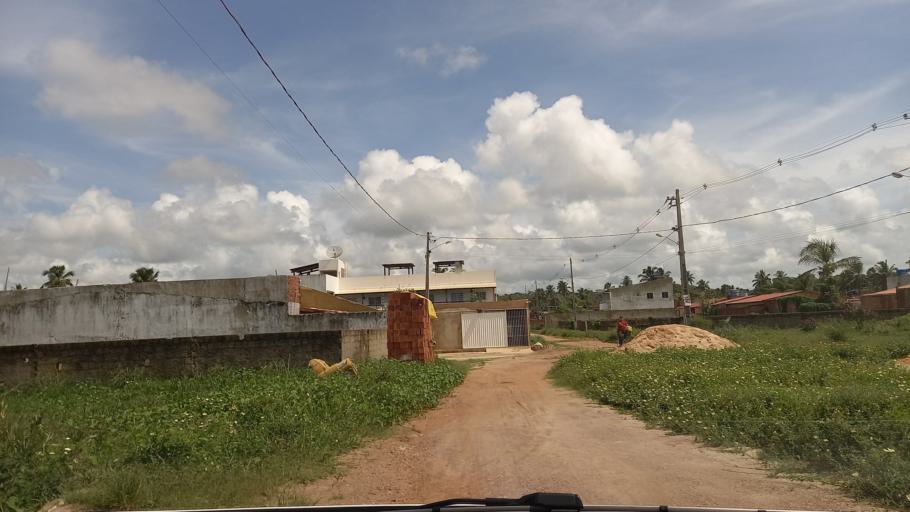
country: BR
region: Pernambuco
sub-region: Sao Jose Da Coroa Grande
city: Sao Jose da Coroa Grande
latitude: -8.9219
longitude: -35.1622
